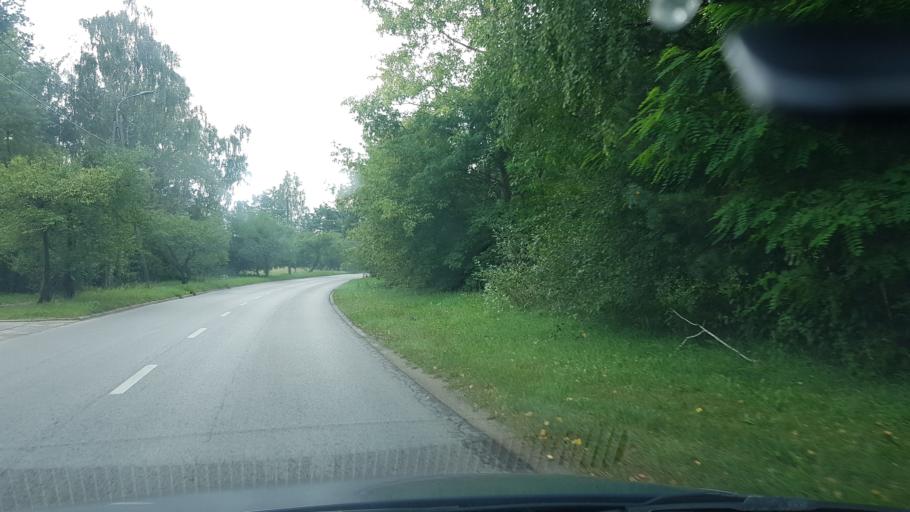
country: PL
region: Masovian Voivodeship
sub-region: Powiat piaseczynski
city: Konstancin-Jeziorna
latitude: 52.0697
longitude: 21.0998
